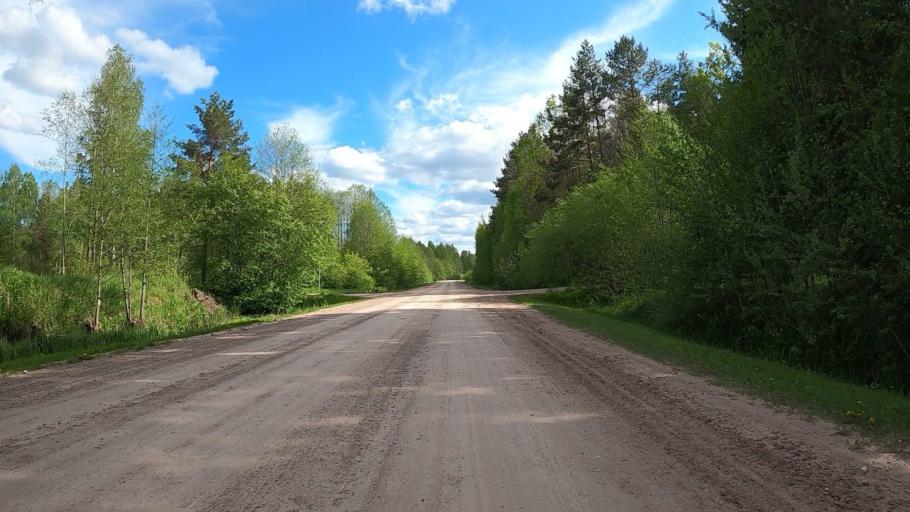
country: LV
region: Jurmala
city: Jurmala
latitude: 56.8630
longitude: 23.7878
